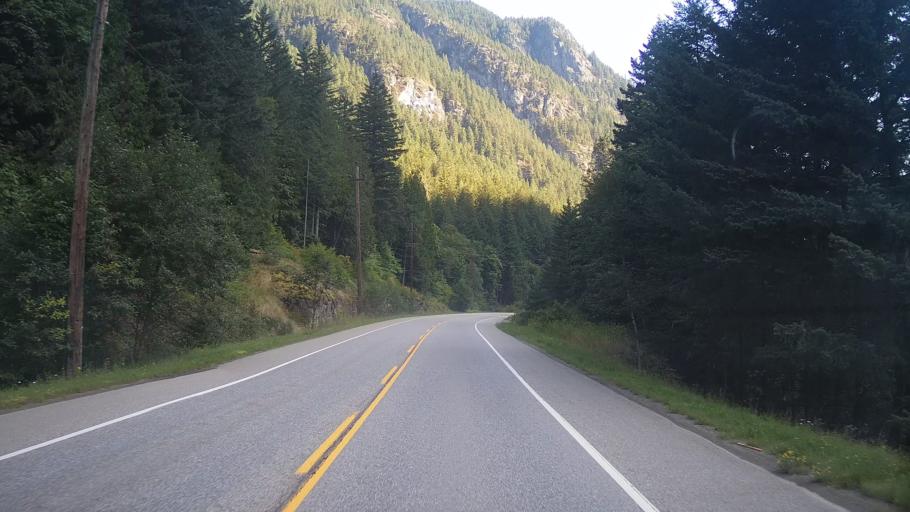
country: CA
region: British Columbia
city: Hope
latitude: 49.6080
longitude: -121.4154
